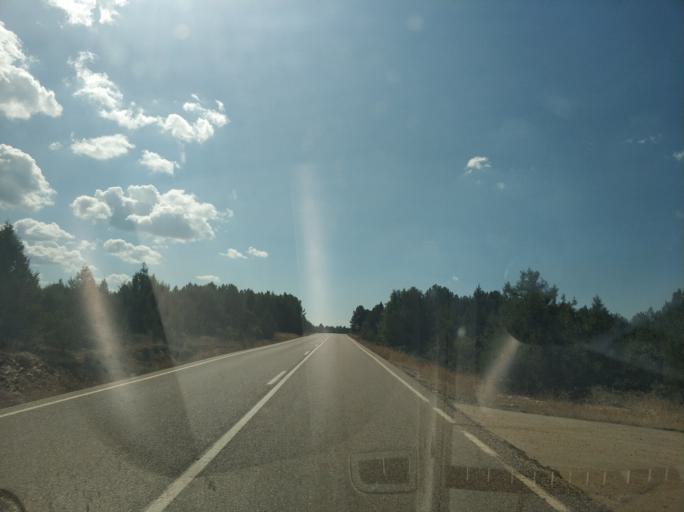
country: ES
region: Castille and Leon
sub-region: Provincia de Soria
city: Herrera de Soria
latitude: 41.7688
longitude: -3.0305
